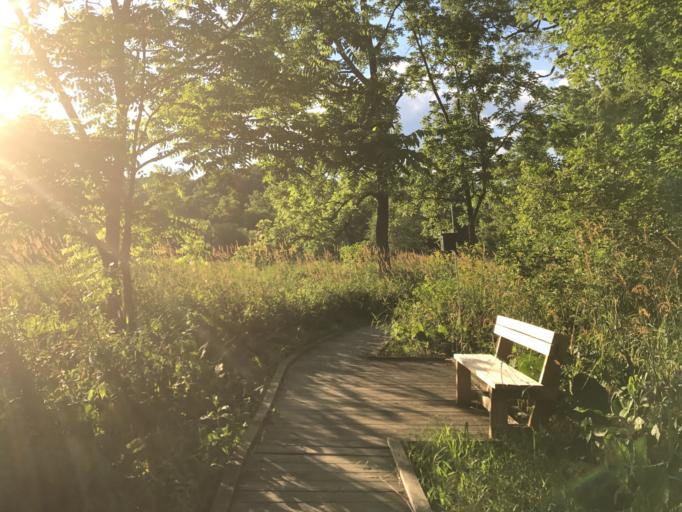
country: US
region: Maryland
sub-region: Harford County
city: Jarrettsville
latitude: 39.6760
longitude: -76.4541
